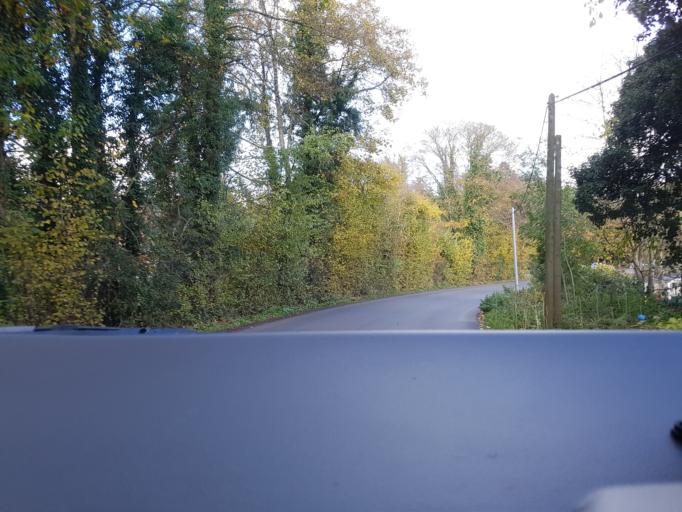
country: FR
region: Lower Normandy
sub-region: Departement de l'Orne
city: Champsecret
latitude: 48.6344
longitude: -0.5524
